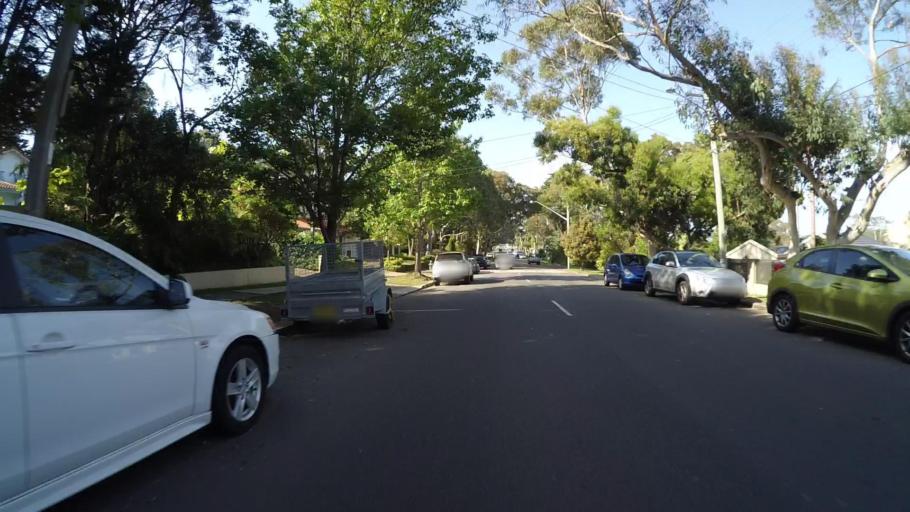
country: AU
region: New South Wales
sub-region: Sutherland Shire
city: Cronulla
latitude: -34.0554
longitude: 151.1399
